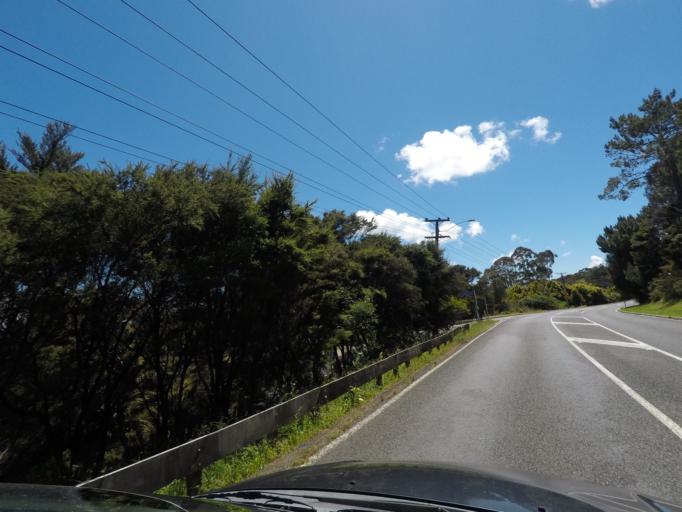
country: NZ
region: Auckland
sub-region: Auckland
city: Rothesay Bay
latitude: -36.7567
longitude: 174.6612
